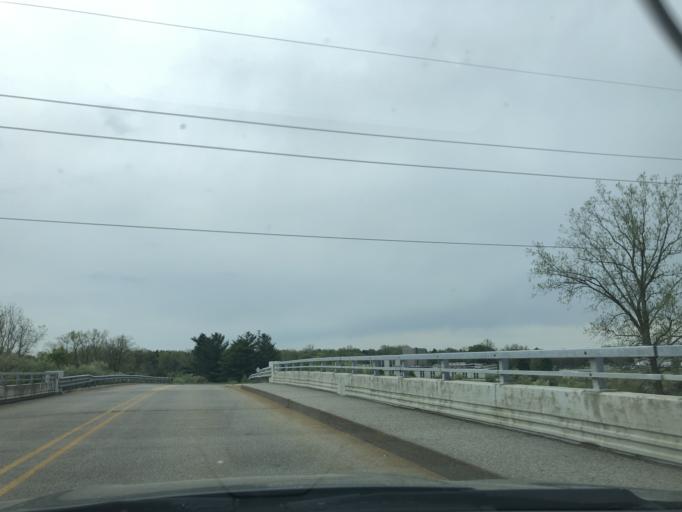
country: US
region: Michigan
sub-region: Eaton County
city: Dimondale
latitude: 42.6736
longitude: -84.6750
